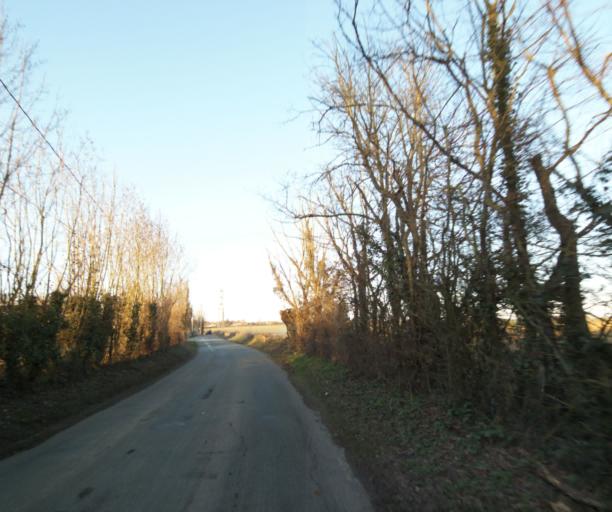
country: FR
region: Poitou-Charentes
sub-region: Departement des Deux-Sevres
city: Niort
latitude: 46.3619
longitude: -0.4518
